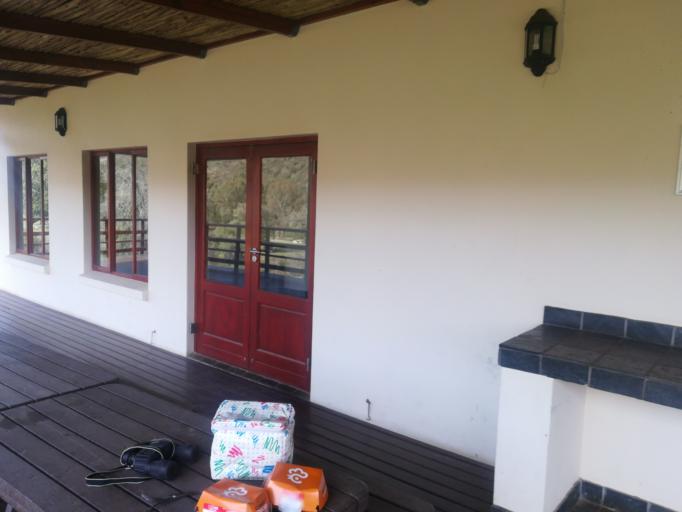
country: ZA
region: Western Cape
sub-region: Overberg District Municipality
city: Swellendam
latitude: -34.0766
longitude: 20.4307
